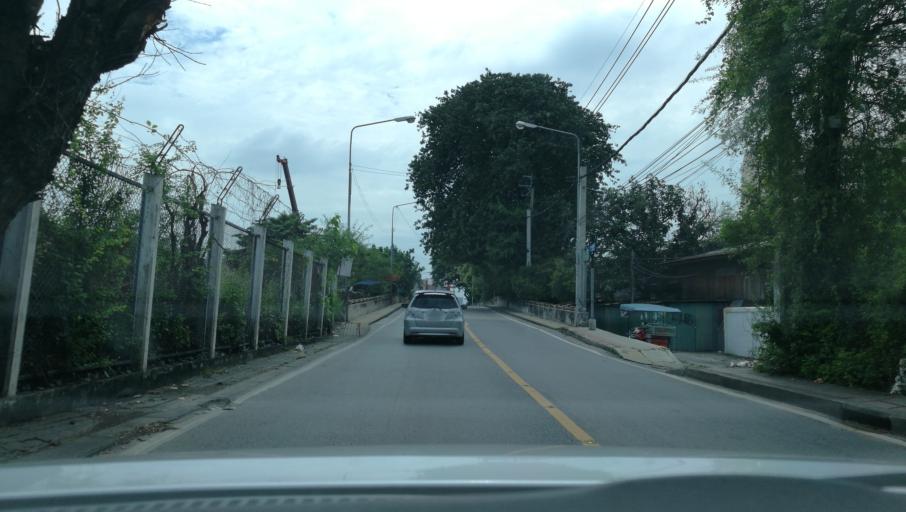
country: TH
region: Bangkok
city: Bang Sue
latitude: 13.7985
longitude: 100.5375
